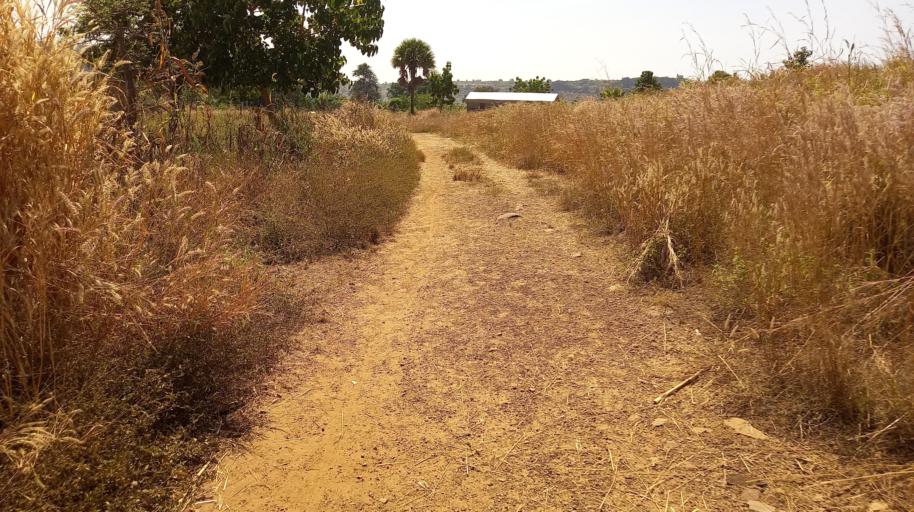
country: TG
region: Savanes
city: Dapaong
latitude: 10.7143
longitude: 0.2748
